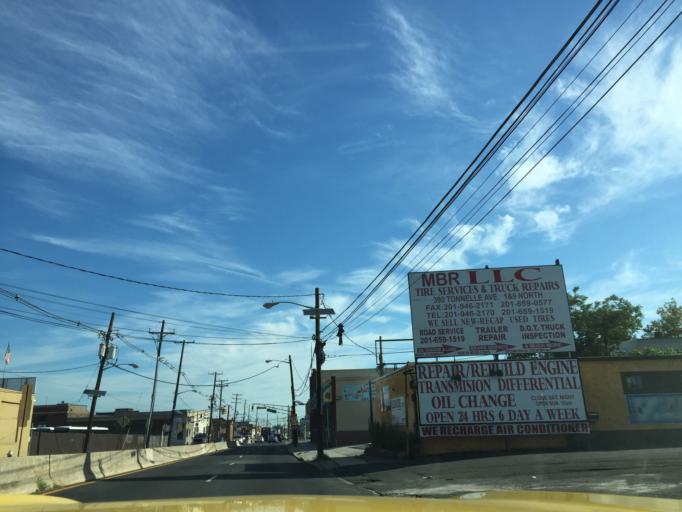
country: US
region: New Jersey
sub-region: Hudson County
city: Jersey City
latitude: 40.7444
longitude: -74.0626
